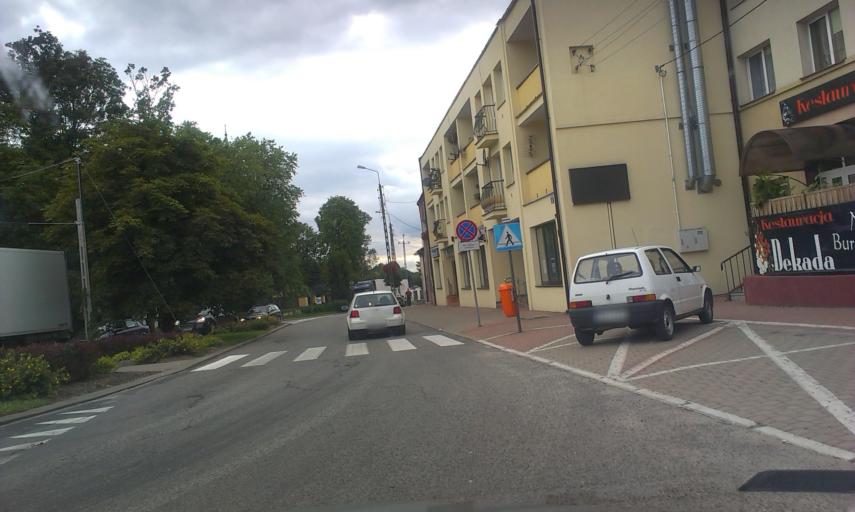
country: PL
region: Masovian Voivodeship
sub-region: Powiat zyrardowski
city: Mszczonow
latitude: 51.9745
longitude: 20.5127
